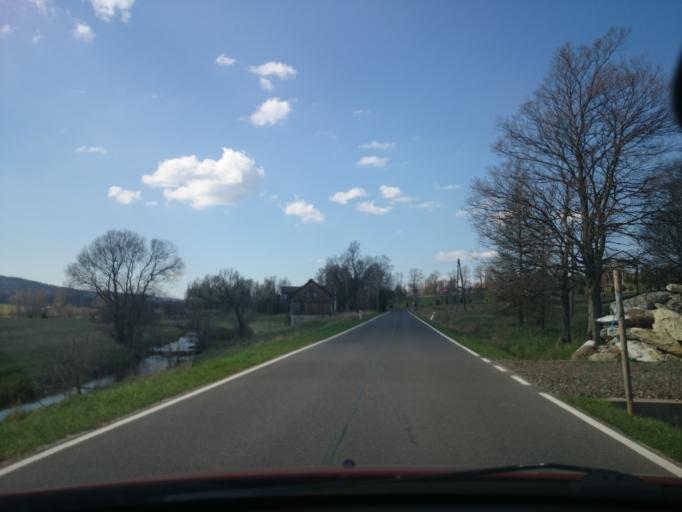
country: PL
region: Lower Silesian Voivodeship
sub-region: Powiat klodzki
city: Szczytna
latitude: 50.3021
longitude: 16.4550
